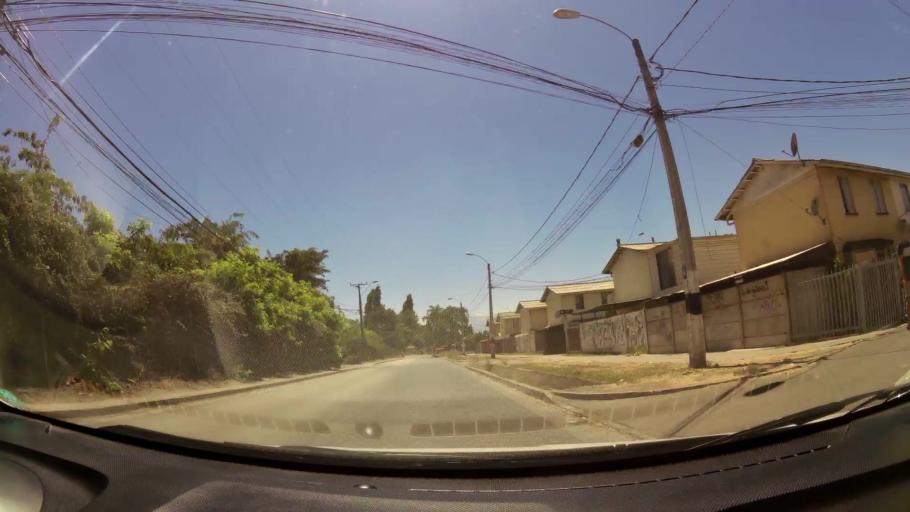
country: CL
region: O'Higgins
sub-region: Provincia de Cachapoal
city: Rancagua
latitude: -34.1549
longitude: -70.7502
